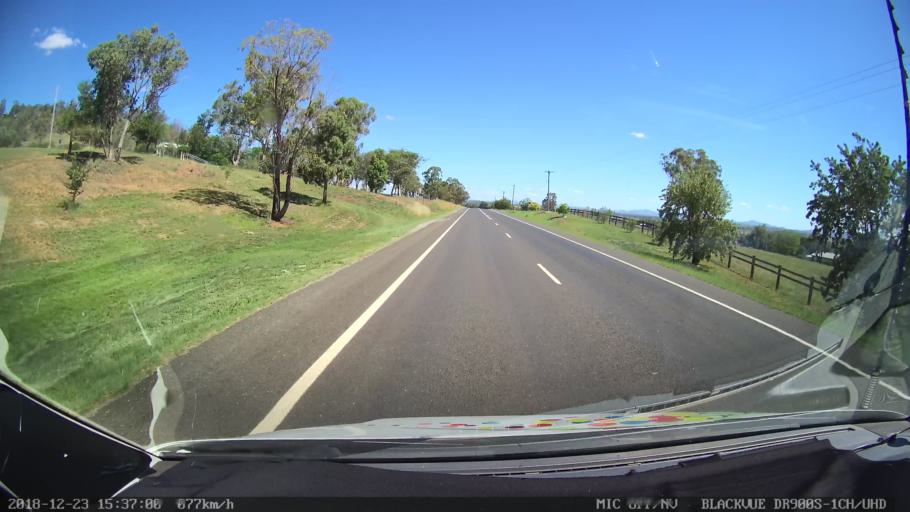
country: AU
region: New South Wales
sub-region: Tamworth Municipality
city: Tamworth
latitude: -31.0474
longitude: 150.8886
